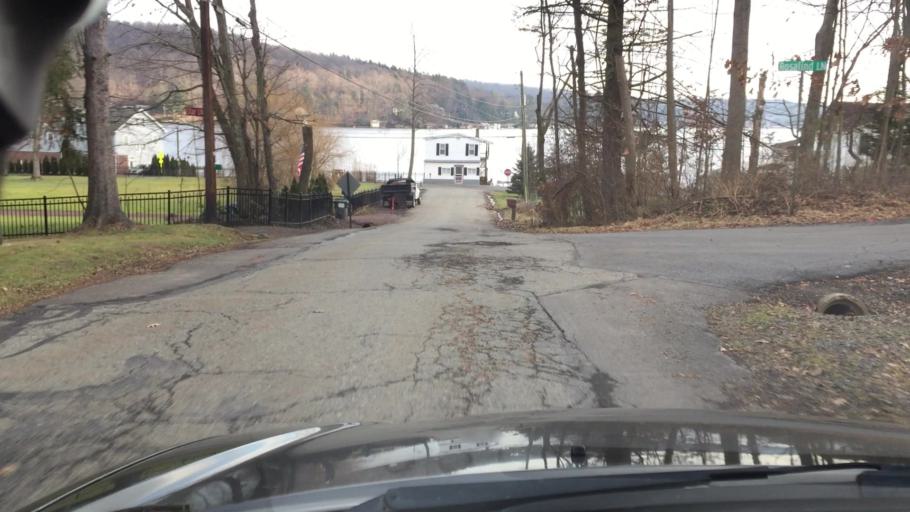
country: US
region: Pennsylvania
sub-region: Luzerne County
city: Harveys Lake
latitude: 41.3739
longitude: -76.0481
